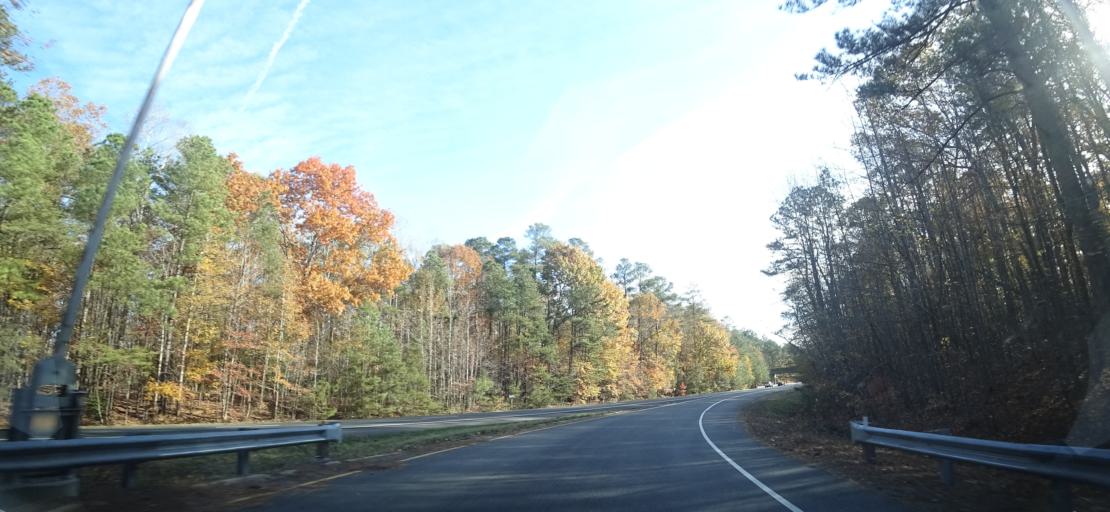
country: US
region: Virginia
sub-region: New Kent County
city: New Kent
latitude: 37.4787
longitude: -76.9222
